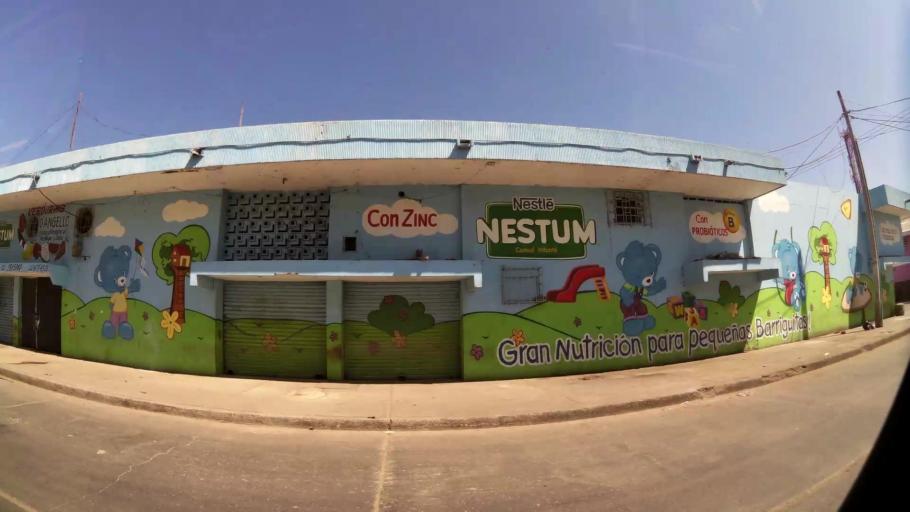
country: CO
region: Atlantico
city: Barranquilla
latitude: 10.9822
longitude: -74.7721
